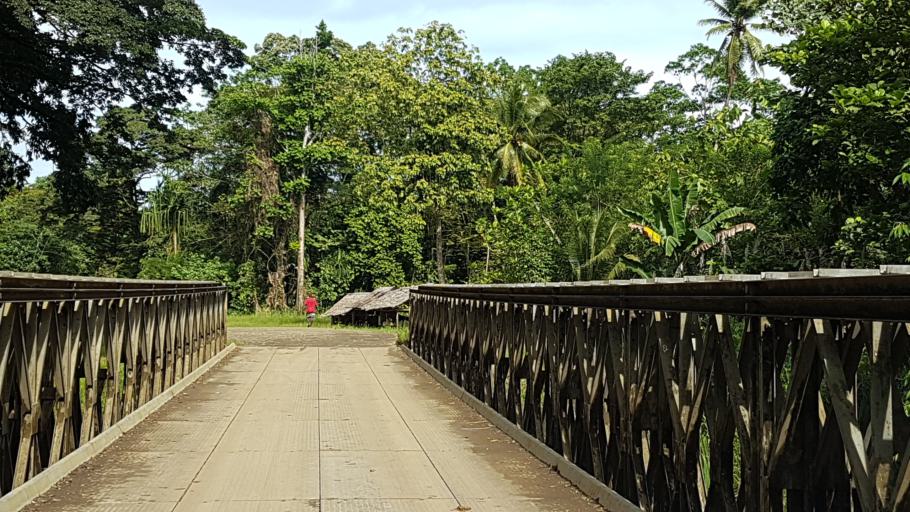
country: PG
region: Milne Bay
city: Alotau
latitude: -10.3386
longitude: 150.6067
